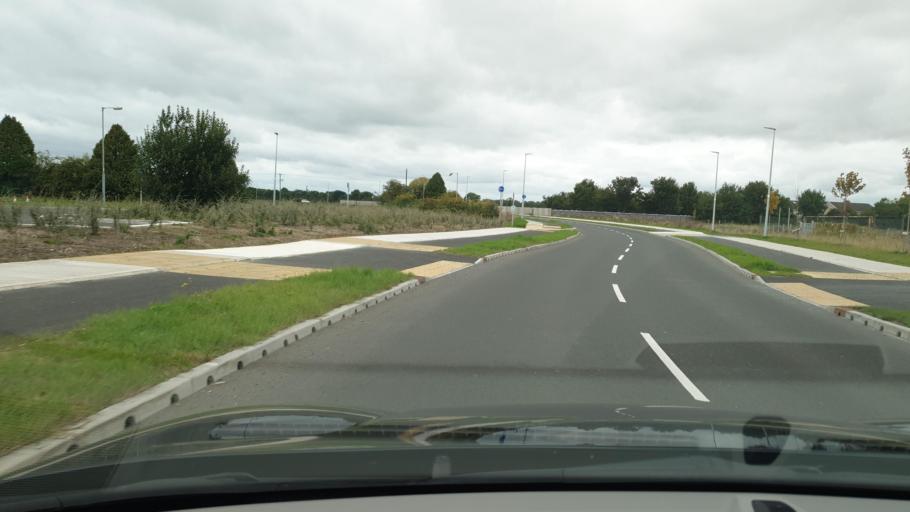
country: IE
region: Leinster
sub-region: Kildare
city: Sallins
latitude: 53.2514
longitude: -6.6698
